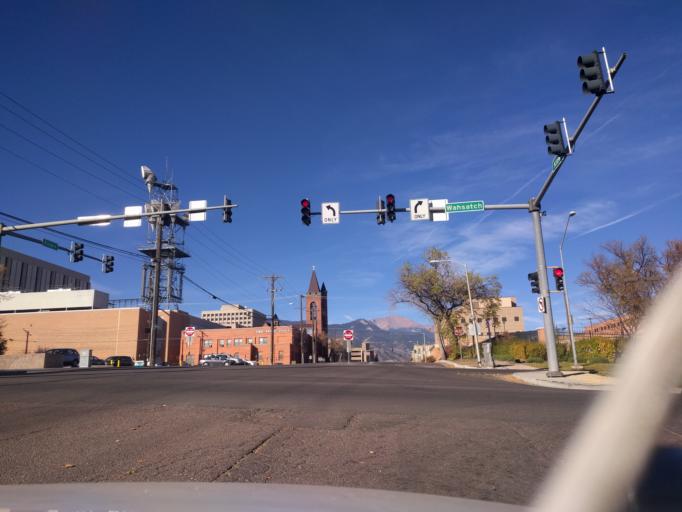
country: US
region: Colorado
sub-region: El Paso County
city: Colorado Springs
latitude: 38.8352
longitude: -104.8177
